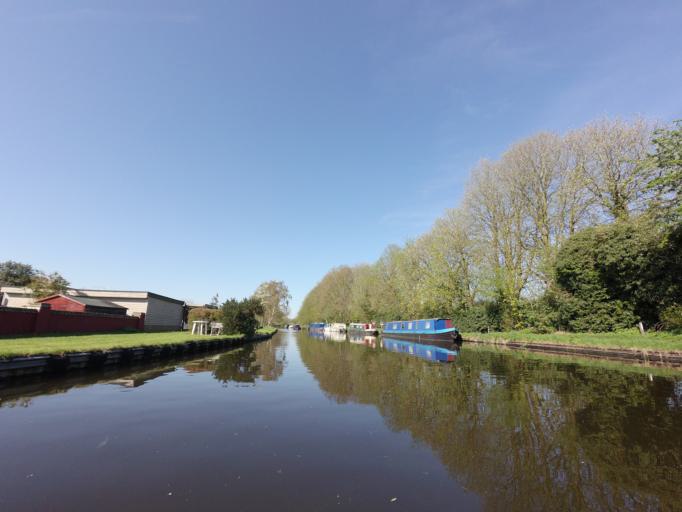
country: GB
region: England
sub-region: Greater London
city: Uxbridge
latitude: 51.5555
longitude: -0.4838
